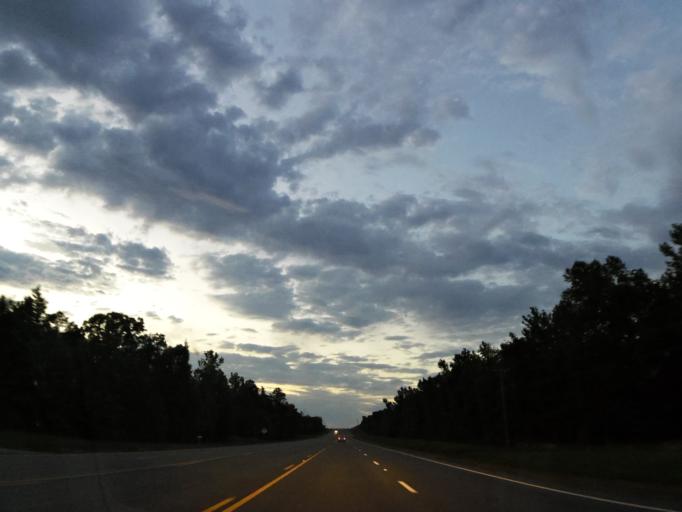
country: US
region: Alabama
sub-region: Marion County
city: Winfield
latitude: 33.9755
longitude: -87.7744
